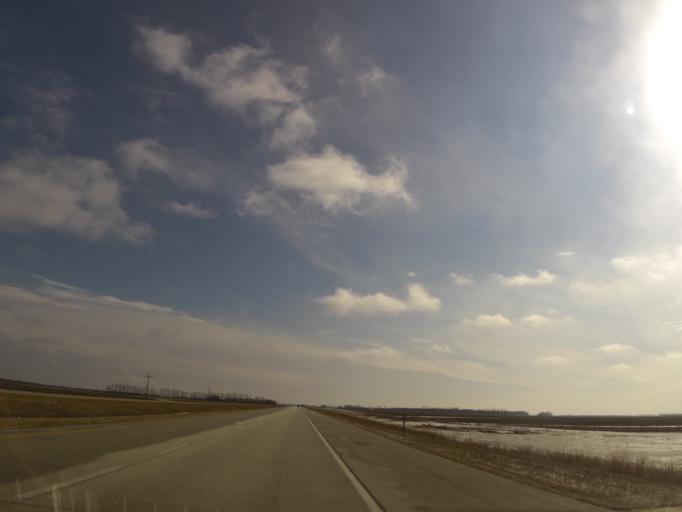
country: US
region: North Dakota
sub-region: Walsh County
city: Grafton
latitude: 48.3229
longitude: -97.1898
